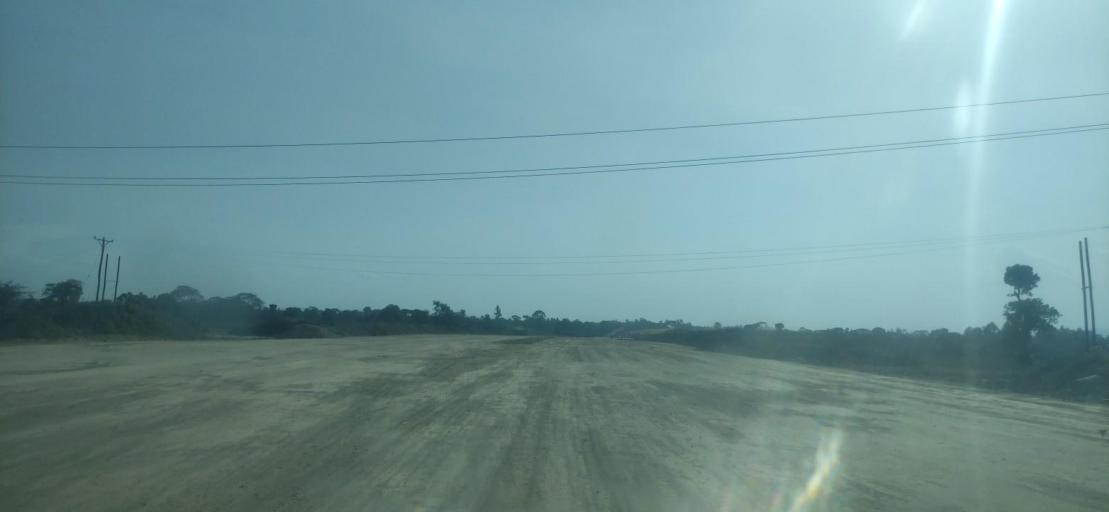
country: ET
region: Oromiya
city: Shashemene
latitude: 7.2550
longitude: 38.5934
